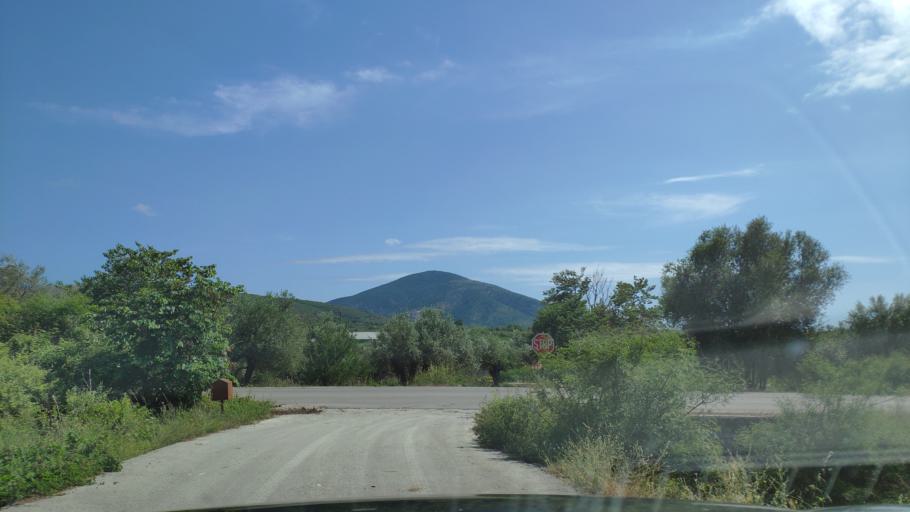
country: AL
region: Vlore
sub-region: Rrethi i Sarandes
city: Konispol
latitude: 39.6203
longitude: 20.2005
